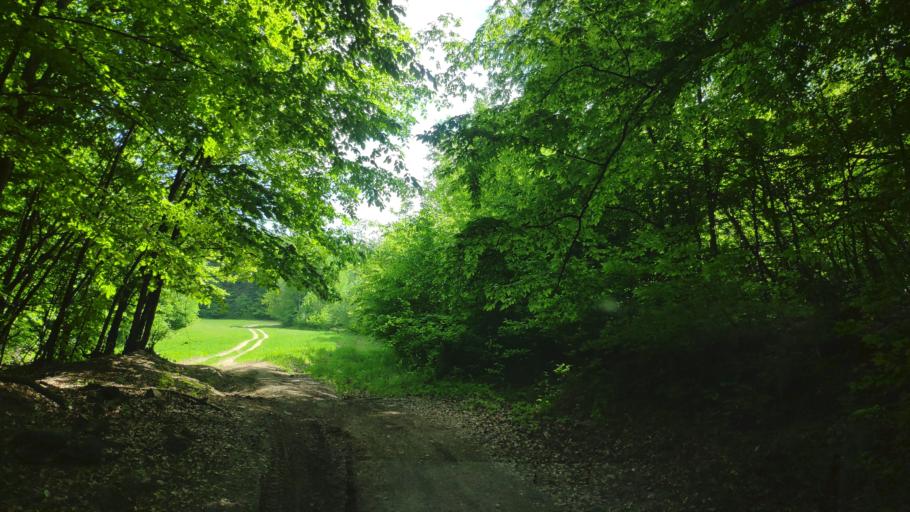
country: SK
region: Presovsky
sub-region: Okres Presov
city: Presov
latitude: 48.9433
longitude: 21.1141
